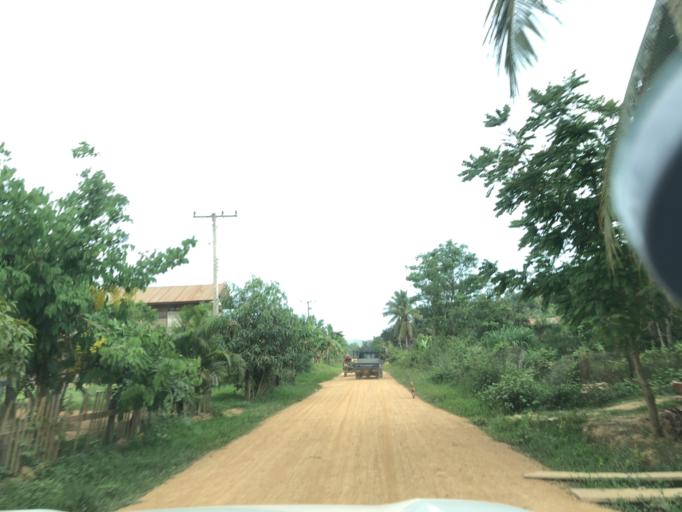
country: TH
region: Loei
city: Chiang Khan
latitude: 18.0168
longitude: 101.4192
